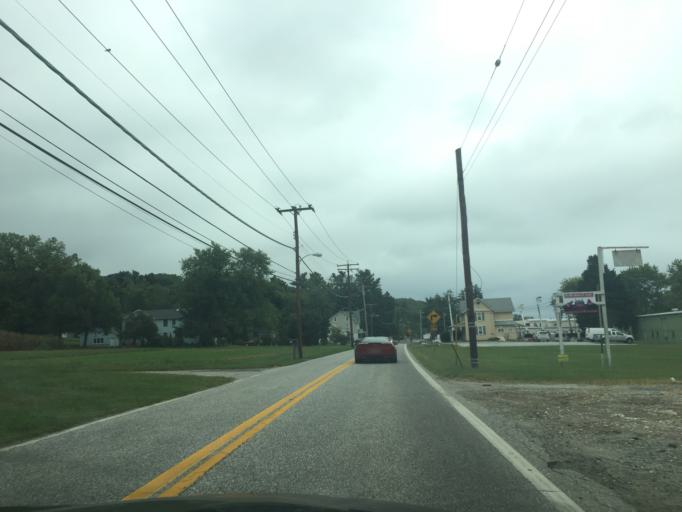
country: US
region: Maryland
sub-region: Baltimore County
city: Perry Hall
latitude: 39.4547
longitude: -76.4997
